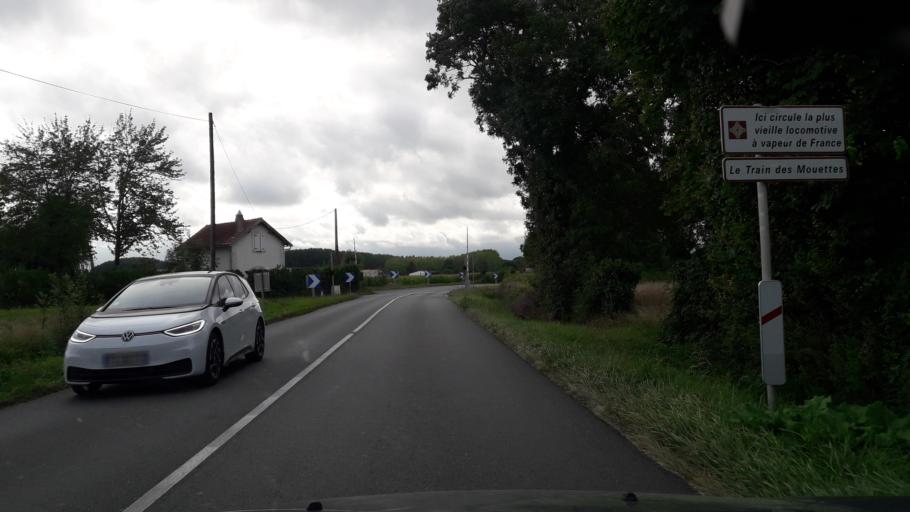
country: FR
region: Poitou-Charentes
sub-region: Departement de la Charente-Maritime
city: Medis
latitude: 45.6750
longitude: -0.9750
